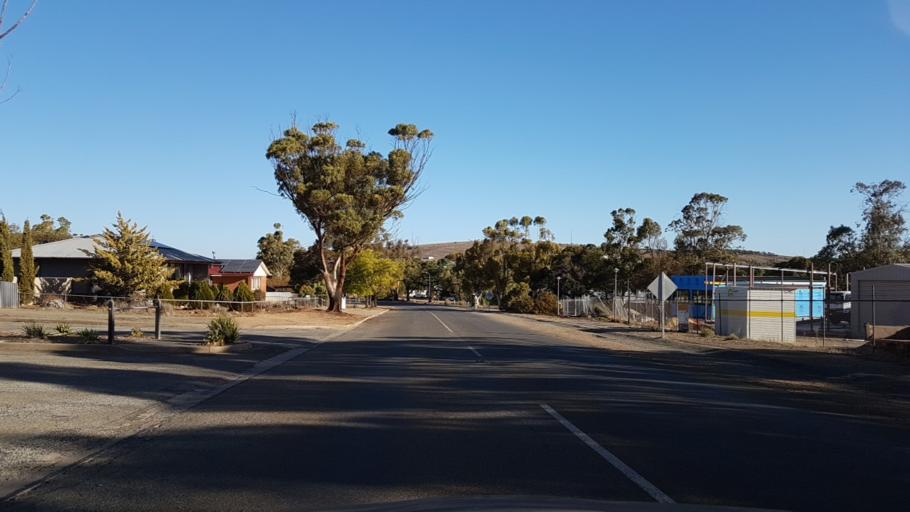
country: AU
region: South Australia
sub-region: Clare and Gilbert Valleys
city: Clare
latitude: -33.6783
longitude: 138.9409
